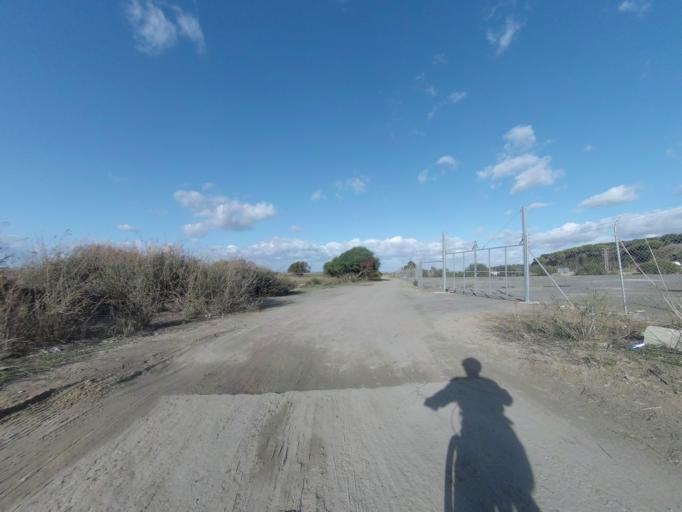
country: ES
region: Andalusia
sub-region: Provincia de Huelva
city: Palos de la Frontera
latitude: 37.2438
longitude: -6.8875
